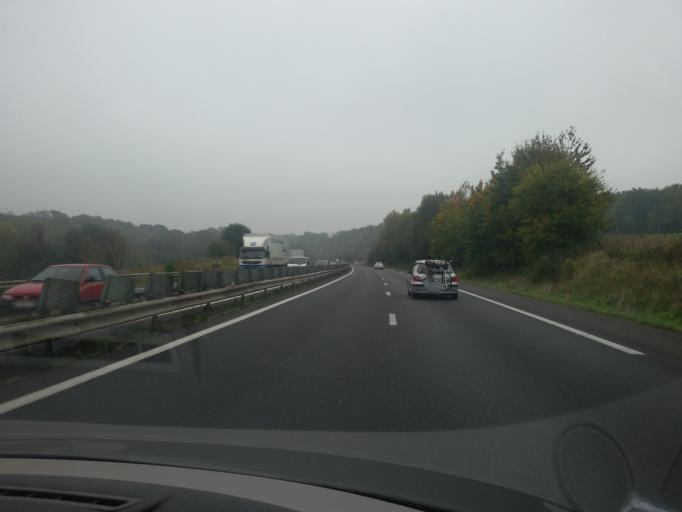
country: FR
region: Lower Normandy
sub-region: Departement du Calvados
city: Dozule
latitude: 49.2465
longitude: 0.0362
